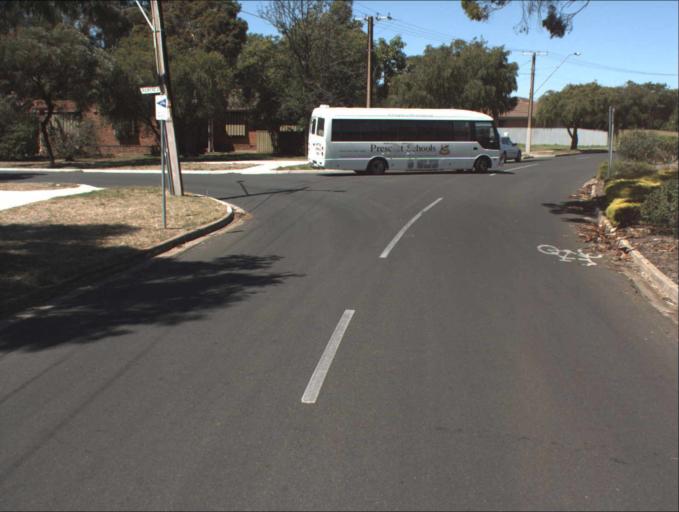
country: AU
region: South Australia
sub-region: Port Adelaide Enfield
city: Enfield
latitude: -34.8549
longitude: 138.6152
